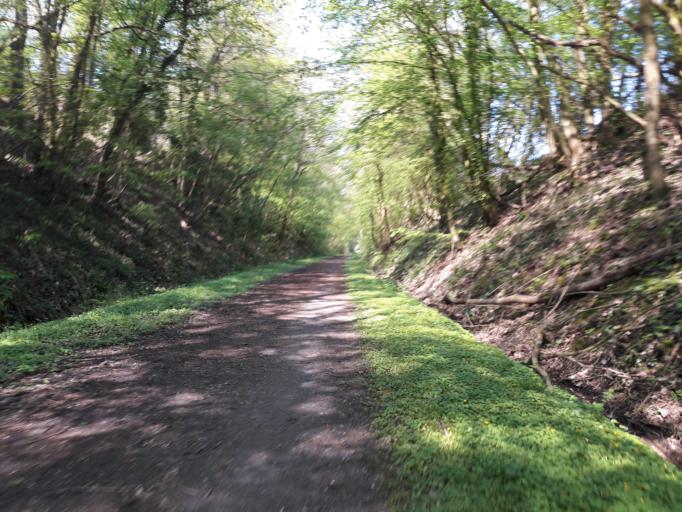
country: FR
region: Nord-Pas-de-Calais
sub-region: Departement du Nord
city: Sains-du-Nord
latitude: 50.1601
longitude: 4.0709
